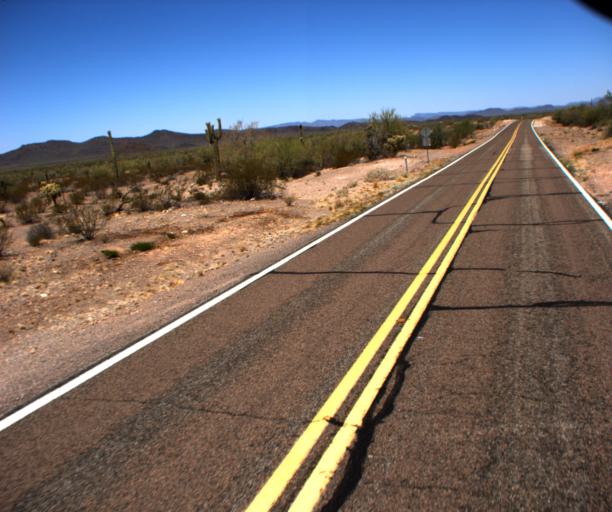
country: US
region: Arizona
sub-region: Pima County
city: Ajo
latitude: 32.2233
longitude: -112.6993
